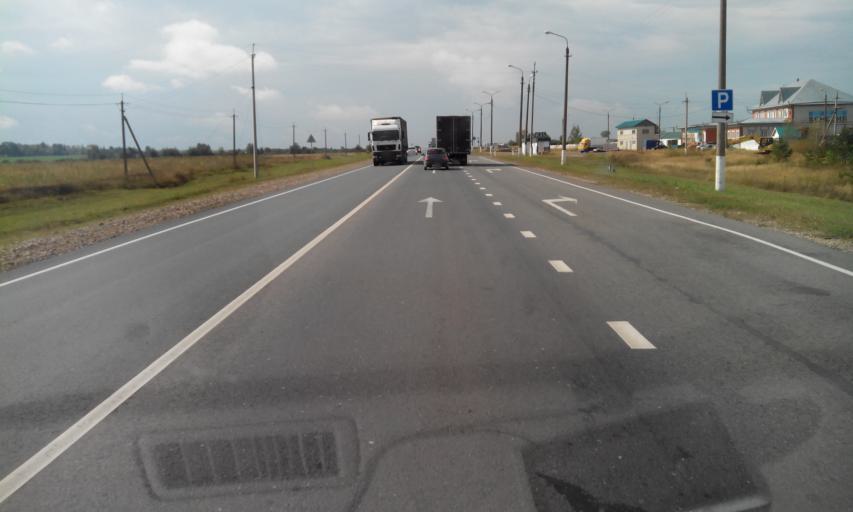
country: RU
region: Penza
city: Kuznetsk
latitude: 53.0844
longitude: 46.6164
